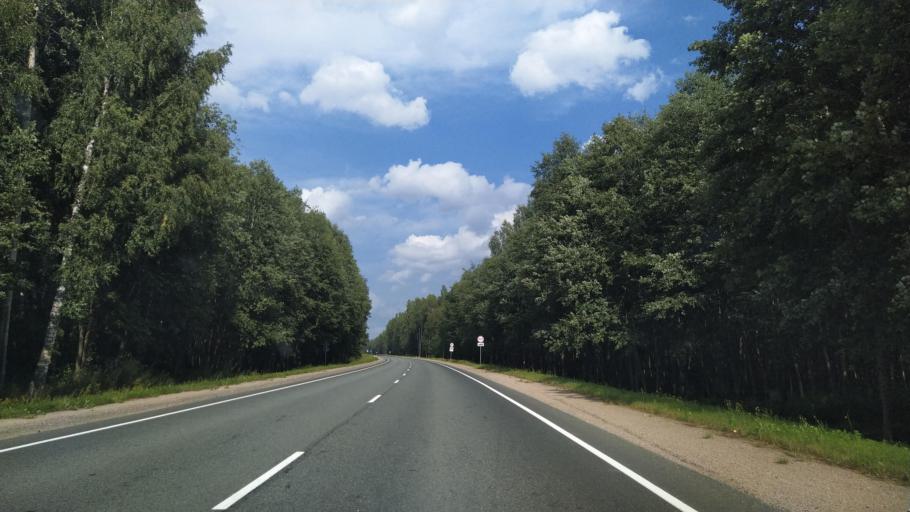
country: RU
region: Pskov
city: Porkhov
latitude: 57.8660
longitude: 29.6022
